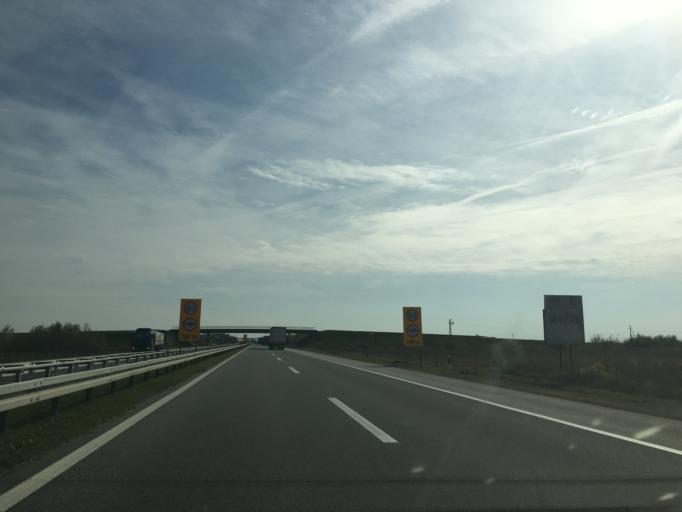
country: RS
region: Autonomna Pokrajina Vojvodina
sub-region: Sremski Okrug
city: Stara Pazova
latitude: 45.0127
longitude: 20.1979
